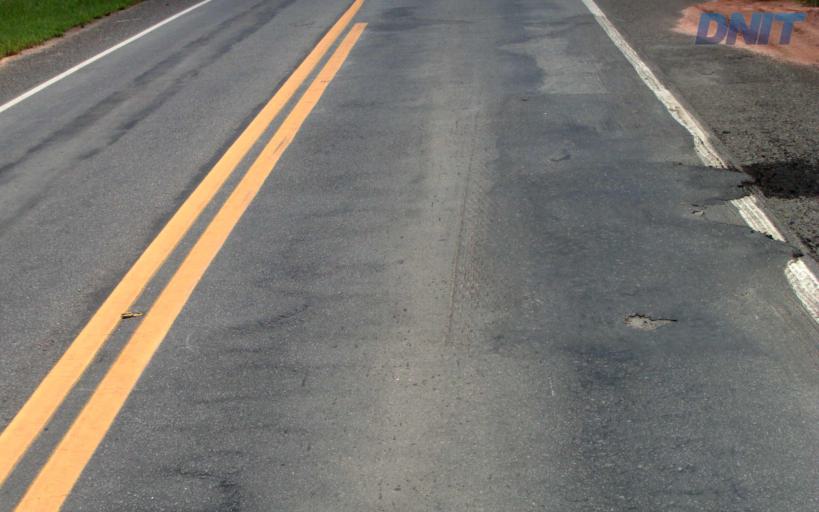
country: BR
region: Minas Gerais
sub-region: Governador Valadares
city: Governador Valadares
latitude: -19.0297
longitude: -42.1480
